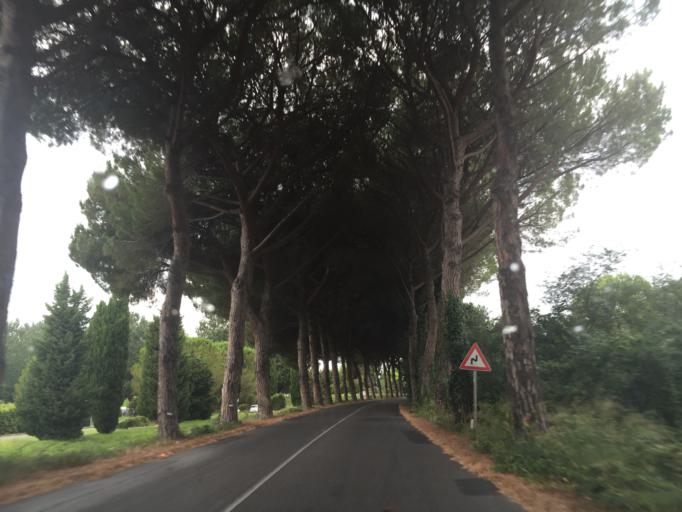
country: IT
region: Tuscany
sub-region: Province of Pisa
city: Uliveto Terme
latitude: 43.6903
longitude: 10.5292
